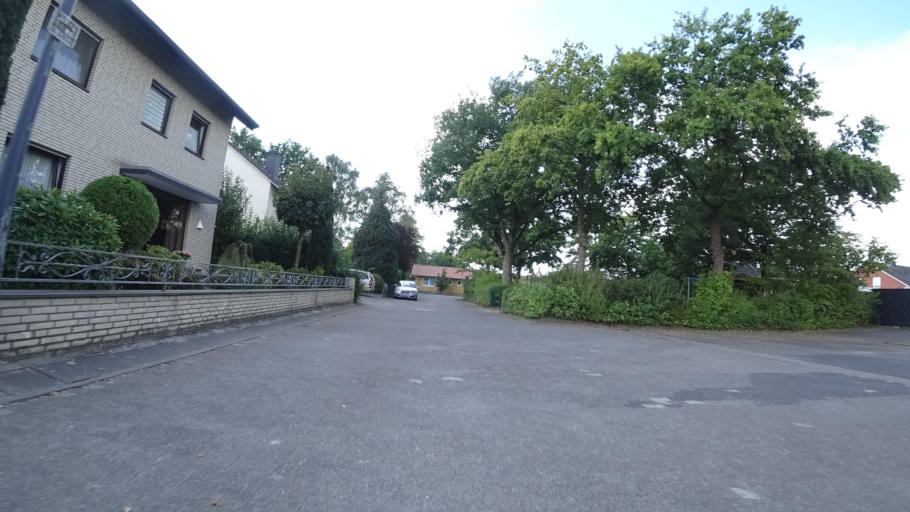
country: DE
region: North Rhine-Westphalia
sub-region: Regierungsbezirk Detmold
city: Guetersloh
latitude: 51.8763
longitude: 8.4311
